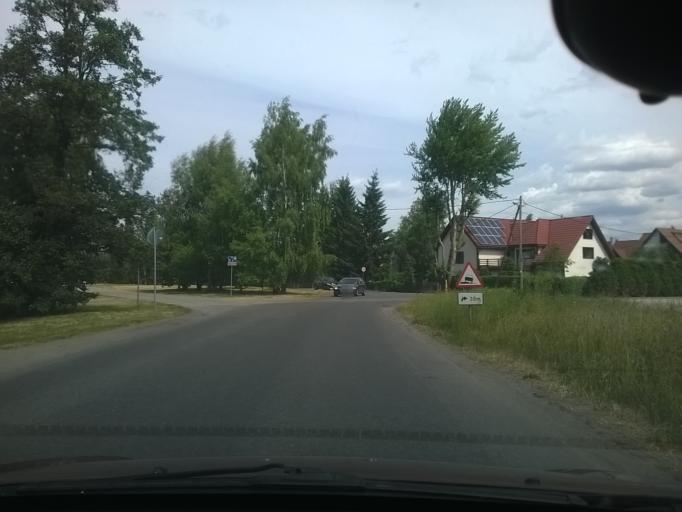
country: EE
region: Harju
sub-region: Tallinna linn
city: Tallinn
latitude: 59.4253
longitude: 24.6893
